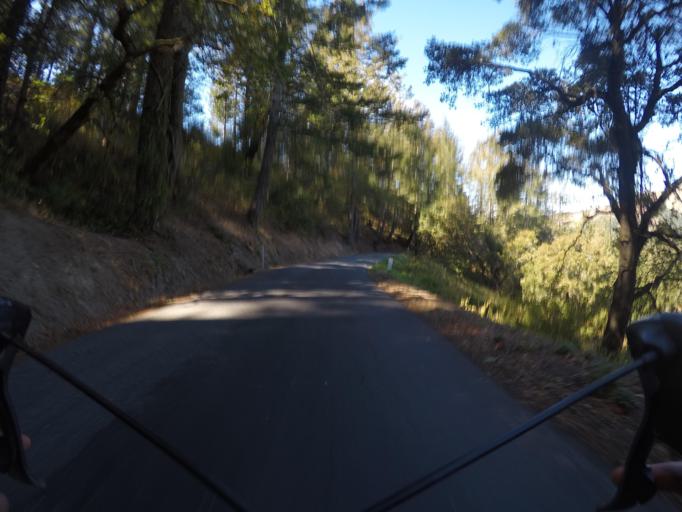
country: US
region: California
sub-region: San Mateo County
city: Portola Valley
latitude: 37.2897
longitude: -122.2224
